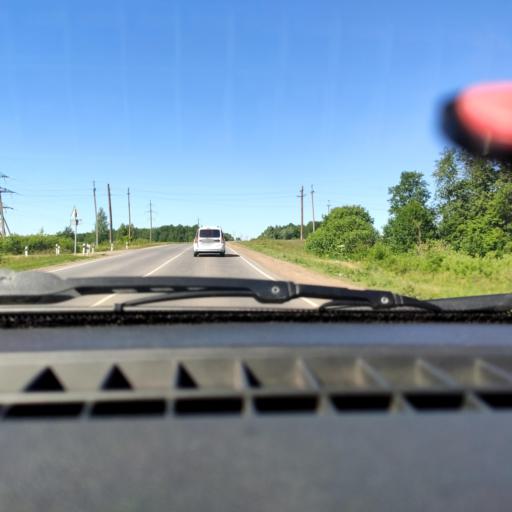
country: RU
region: Bashkortostan
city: Iglino
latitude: 54.8815
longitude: 56.4695
